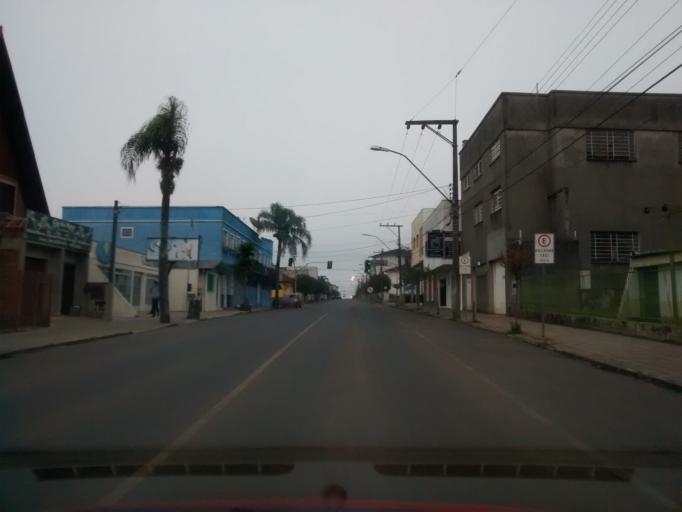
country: BR
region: Rio Grande do Sul
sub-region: Vacaria
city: Vacaria
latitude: -28.5047
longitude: -50.9332
